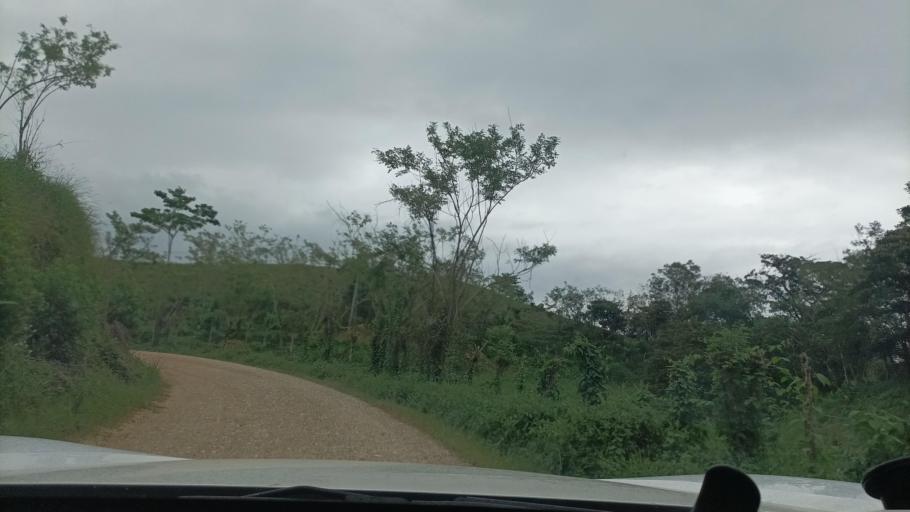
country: MX
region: Veracruz
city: Hidalgotitlan
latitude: 17.6101
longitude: -94.5224
